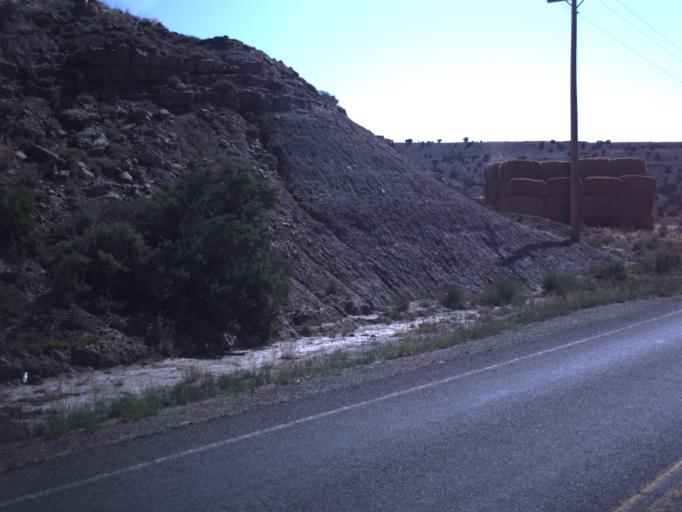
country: US
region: Utah
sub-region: Duchesne County
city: Duchesne
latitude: 40.2606
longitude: -110.4098
